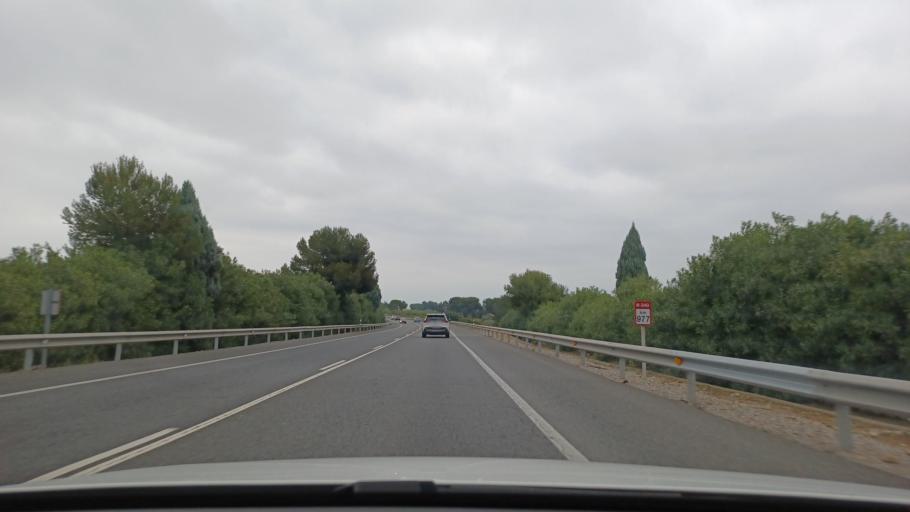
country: ES
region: Valencia
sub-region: Provincia de Castello
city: Borriol
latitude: 40.0044
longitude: -0.0656
